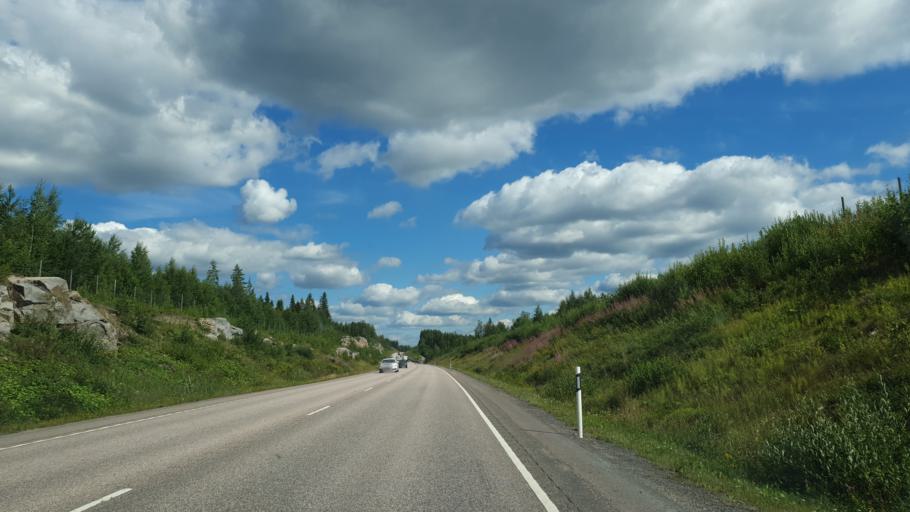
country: FI
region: Pirkanmaa
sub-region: Tampere
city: Kuhmalahti
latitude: 61.7077
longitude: 24.5915
